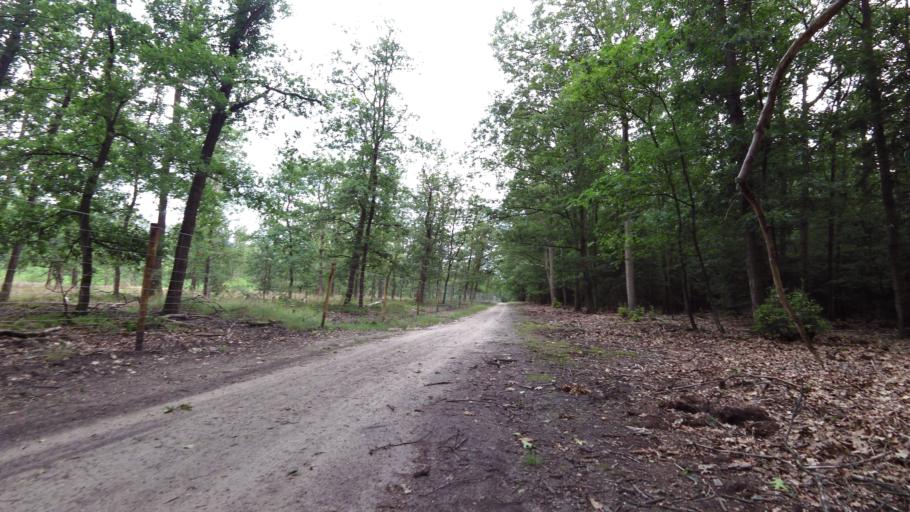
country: NL
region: Gelderland
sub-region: Gemeente Apeldoorn
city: Uddel
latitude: 52.1949
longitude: 5.8487
